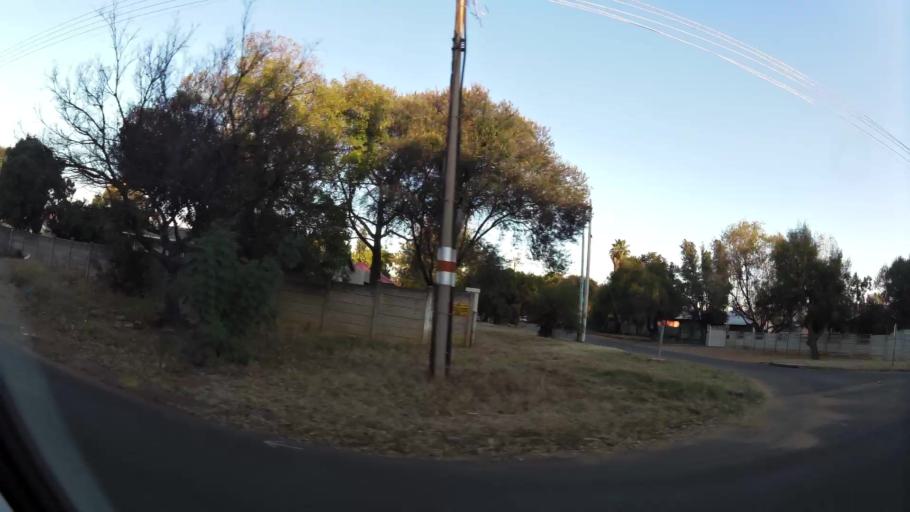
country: ZA
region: North-West
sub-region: Bojanala Platinum District Municipality
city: Rustenburg
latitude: -25.6769
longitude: 27.2208
